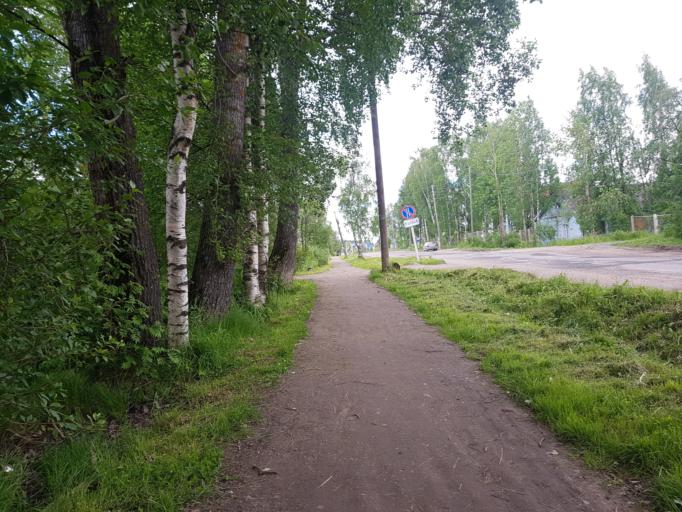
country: RU
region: Republic of Karelia
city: Kalevala
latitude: 65.2031
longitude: 31.1743
